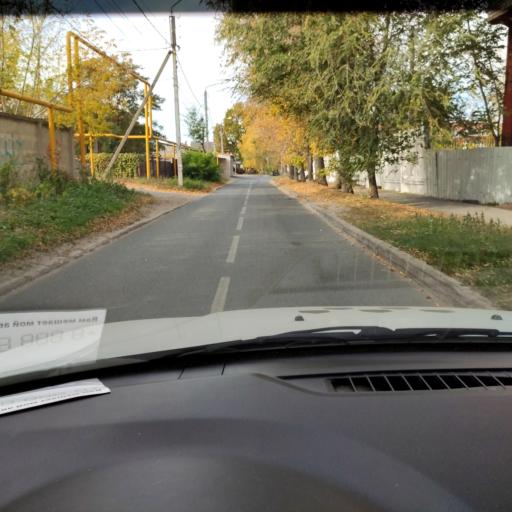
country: RU
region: Samara
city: Tol'yatti
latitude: 53.5132
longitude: 49.4046
